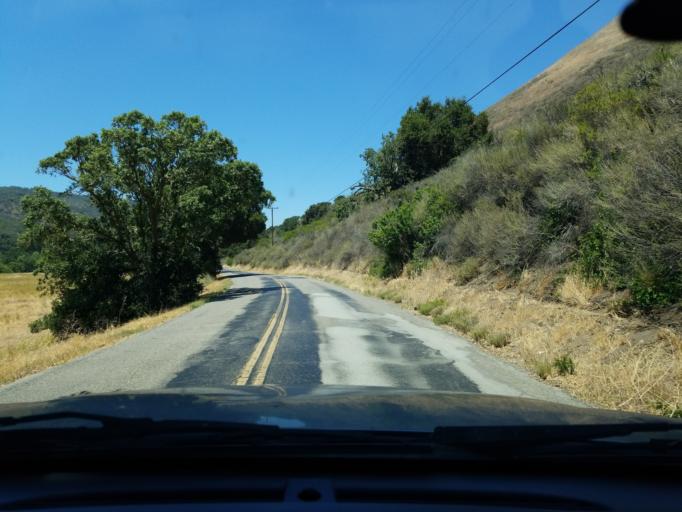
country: US
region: California
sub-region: Monterey County
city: Carmel Valley Village
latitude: 36.4435
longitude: -121.6605
